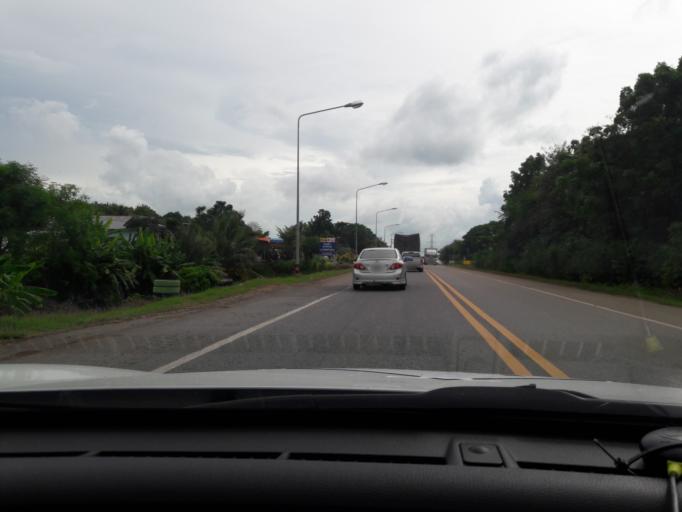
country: TH
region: Nakhon Sawan
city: Tak Fa
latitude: 15.4203
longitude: 100.5166
